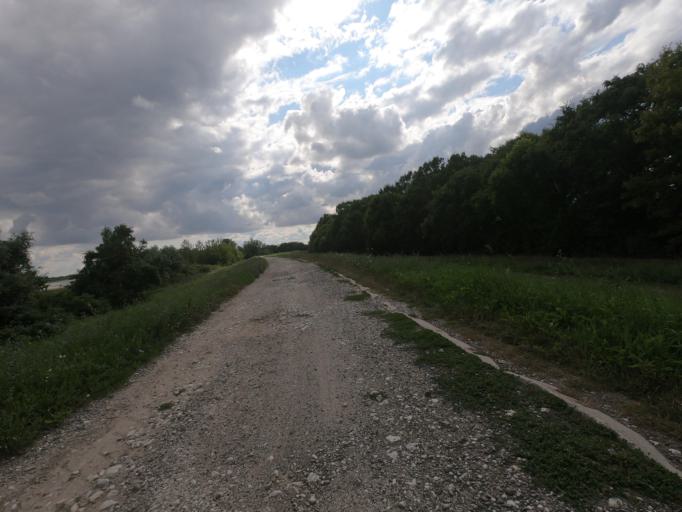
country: HU
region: Heves
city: Poroszlo
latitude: 47.6728
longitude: 20.7025
